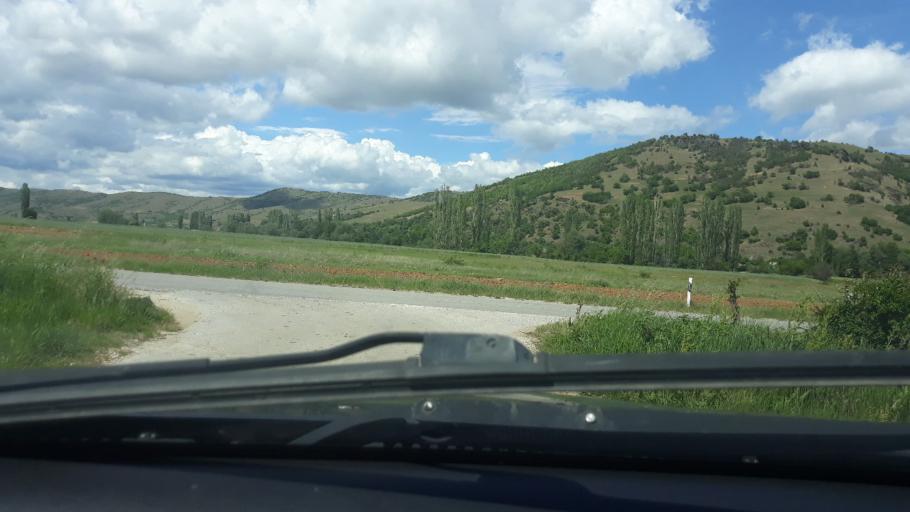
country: MK
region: Krivogastani
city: Krivogashtani
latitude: 41.3530
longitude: 21.2975
